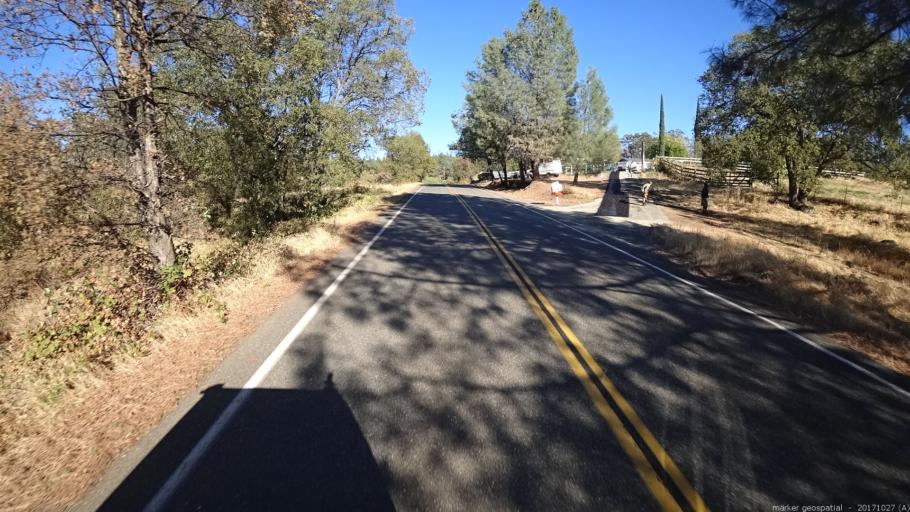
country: US
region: California
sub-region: Shasta County
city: Shingletown
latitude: 40.6162
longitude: -121.9359
